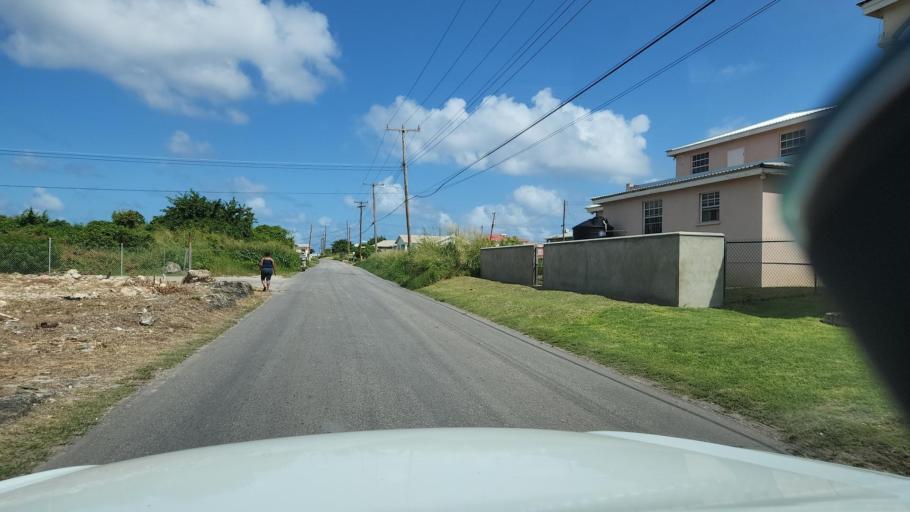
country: BB
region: Saint Philip
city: Crane
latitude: 13.1387
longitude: -59.4348
